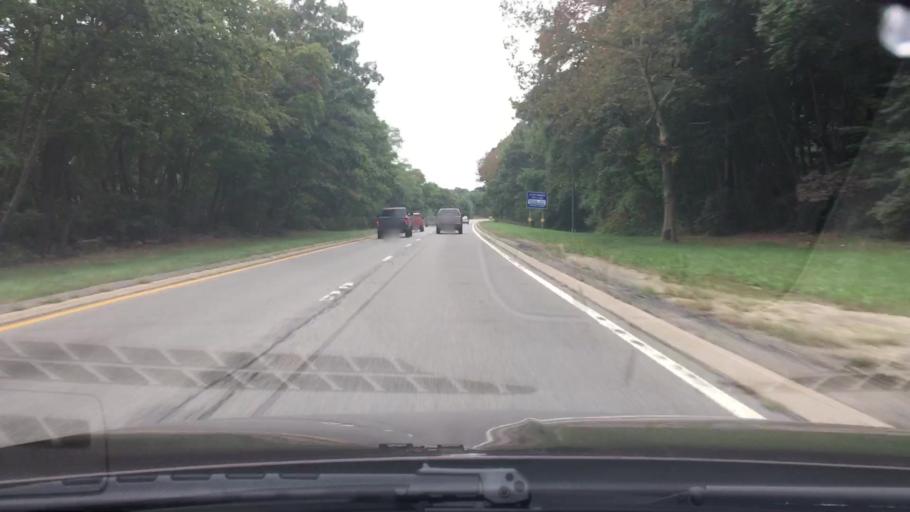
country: US
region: New York
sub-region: Suffolk County
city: Elwood
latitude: 40.8275
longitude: -73.3199
